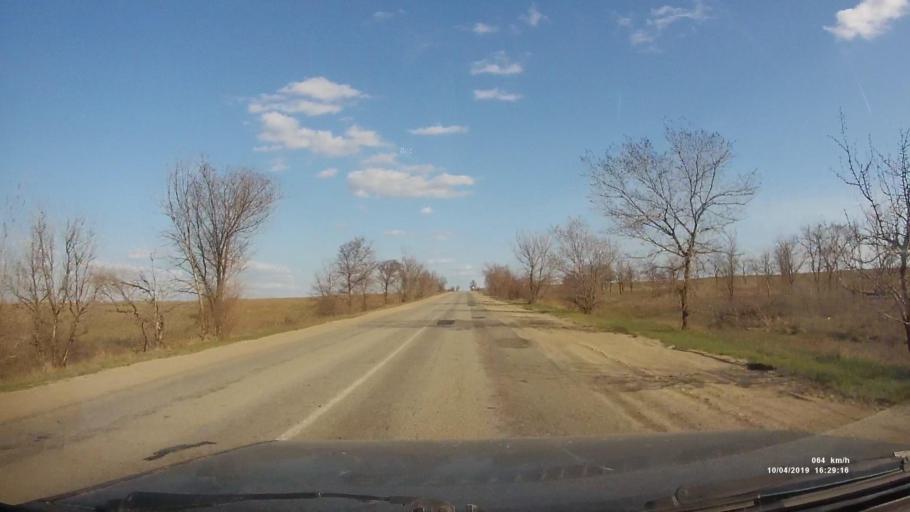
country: RU
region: Rostov
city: Staraya Stanitsa
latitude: 48.2694
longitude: 40.3532
